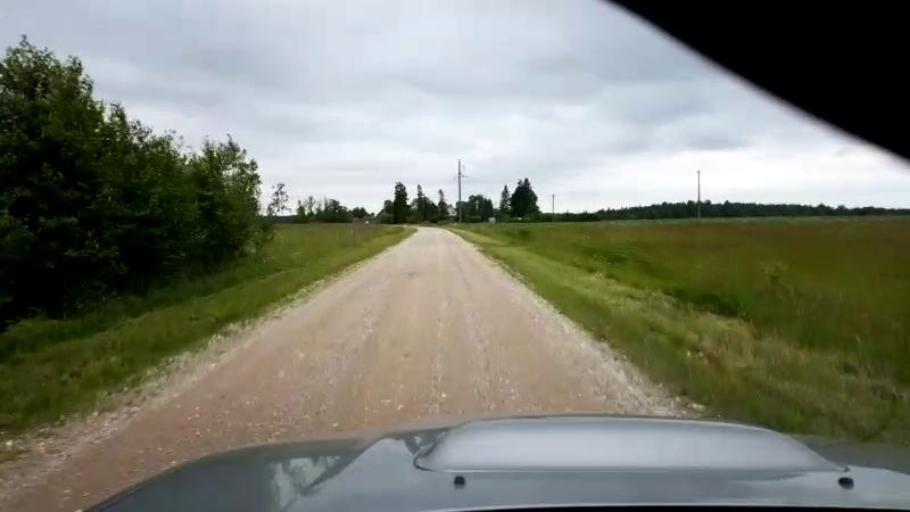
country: EE
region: Paernumaa
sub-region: Halinga vald
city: Parnu-Jaagupi
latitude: 58.5416
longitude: 24.5587
